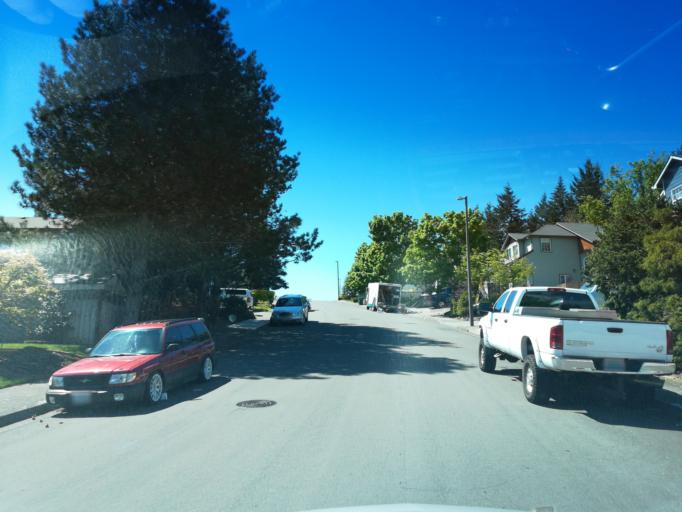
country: US
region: Oregon
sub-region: Multnomah County
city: Troutdale
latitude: 45.5222
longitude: -122.3904
